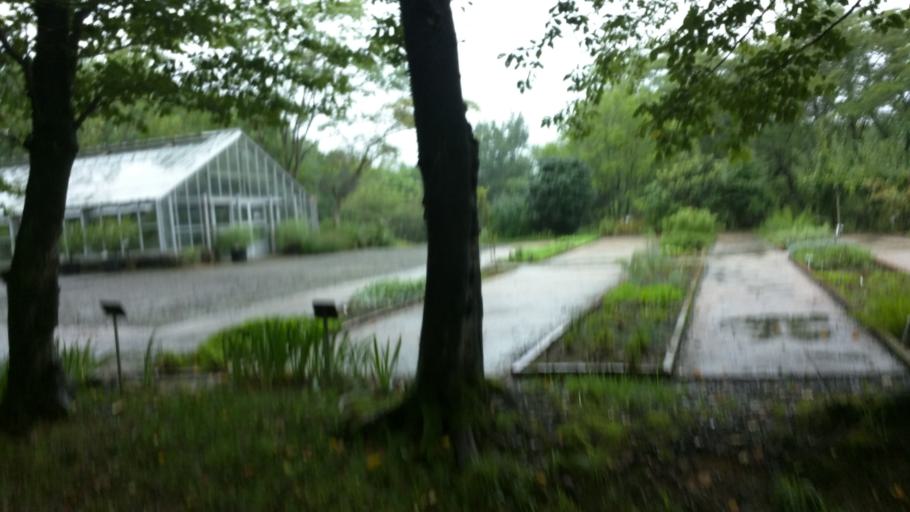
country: JP
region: Fukushima
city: Koriyama
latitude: 37.4124
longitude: 140.2748
